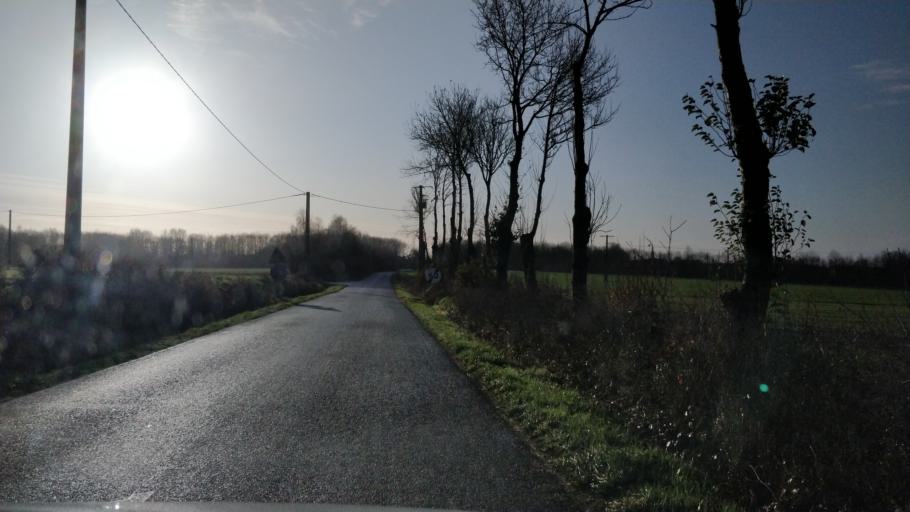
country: FR
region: Brittany
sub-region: Departement d'Ille-et-Vilaine
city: Chavagne
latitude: 48.0621
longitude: -1.7894
